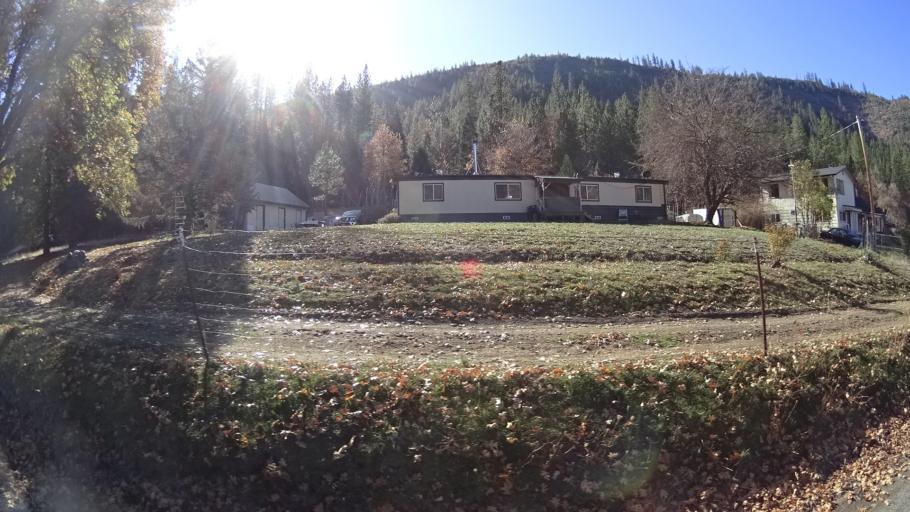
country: US
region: California
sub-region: Siskiyou County
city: Yreka
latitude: 41.8349
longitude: -122.8604
